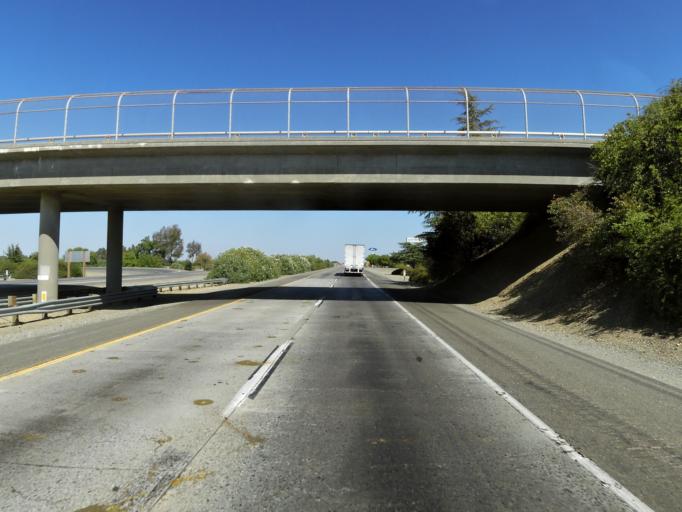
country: US
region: California
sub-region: Tehama County
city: Corning
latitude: 39.9278
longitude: -122.2001
